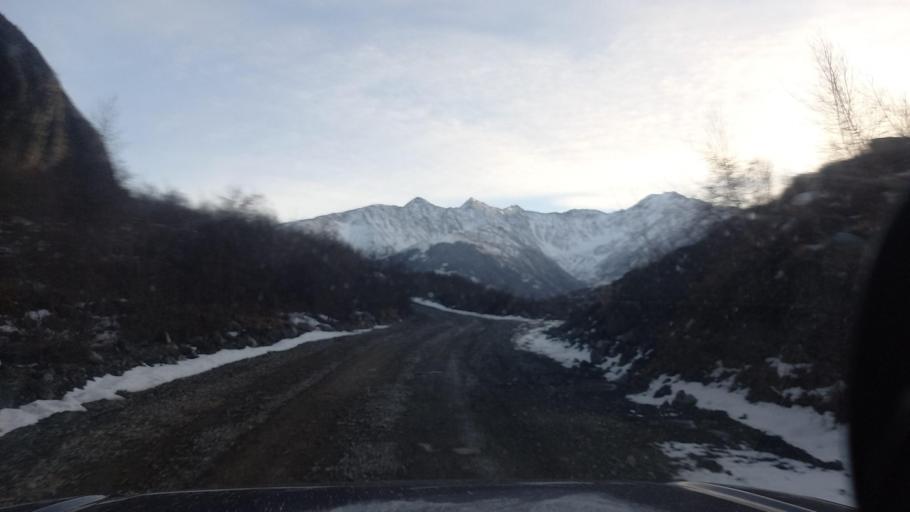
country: RU
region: Ingushetiya
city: Dzhayrakh
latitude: 42.8630
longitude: 44.5202
